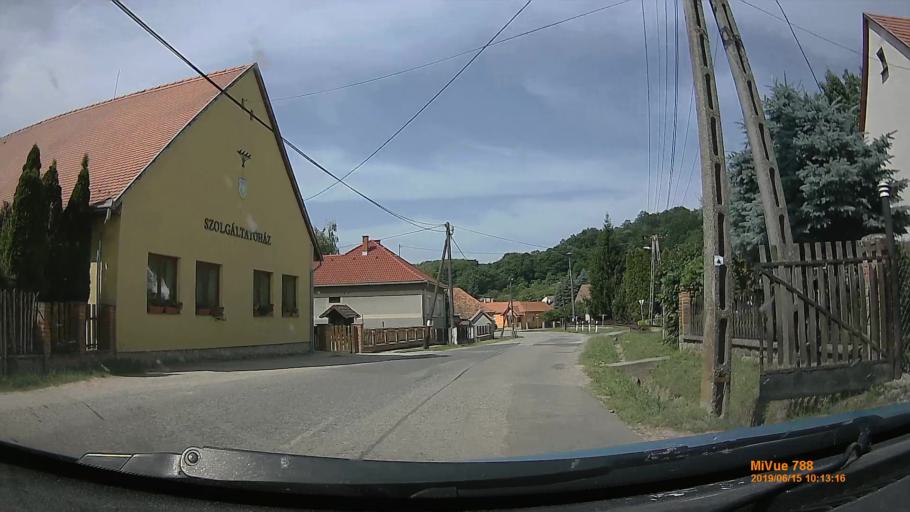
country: HU
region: Baranya
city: Buekkoesd
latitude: 46.1343
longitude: 18.0453
